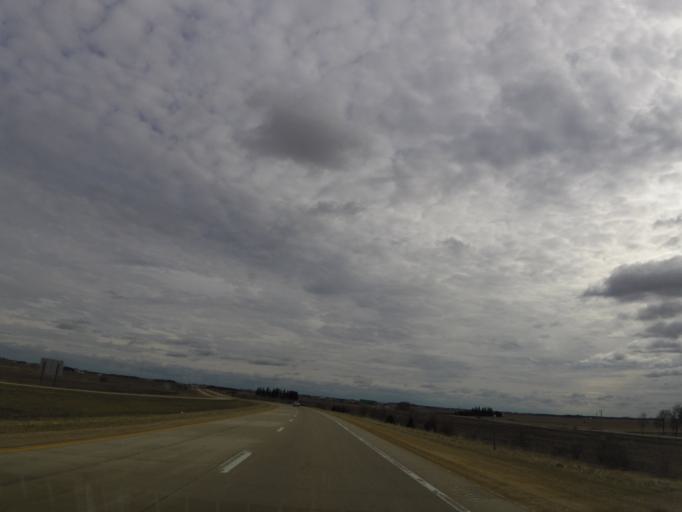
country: US
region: Iowa
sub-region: Chickasaw County
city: New Hampton
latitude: 43.0547
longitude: -92.3361
